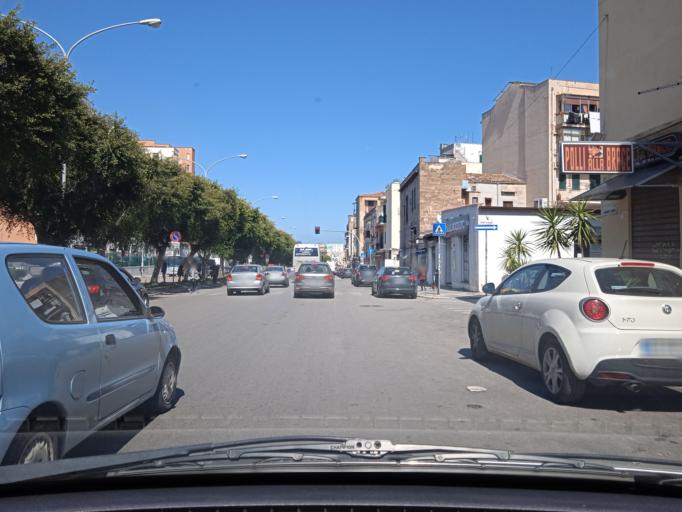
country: IT
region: Sicily
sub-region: Palermo
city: Palermo
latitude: 38.1053
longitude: 13.3516
